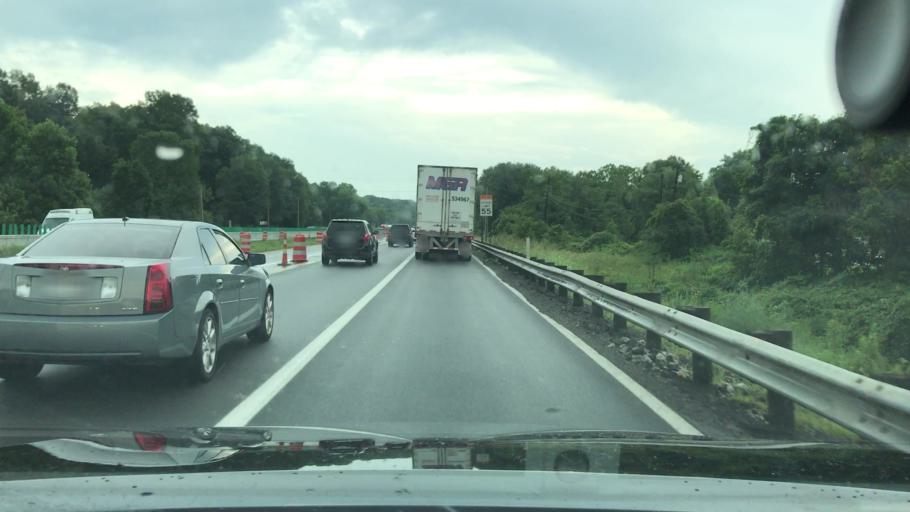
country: US
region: West Virginia
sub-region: Kanawha County
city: Nitro
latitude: 38.4552
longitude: -81.8768
